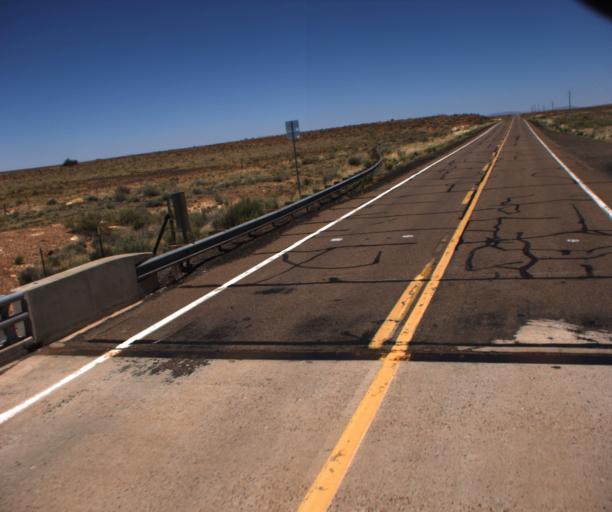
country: US
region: Arizona
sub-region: Coconino County
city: LeChee
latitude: 34.9067
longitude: -110.8429
